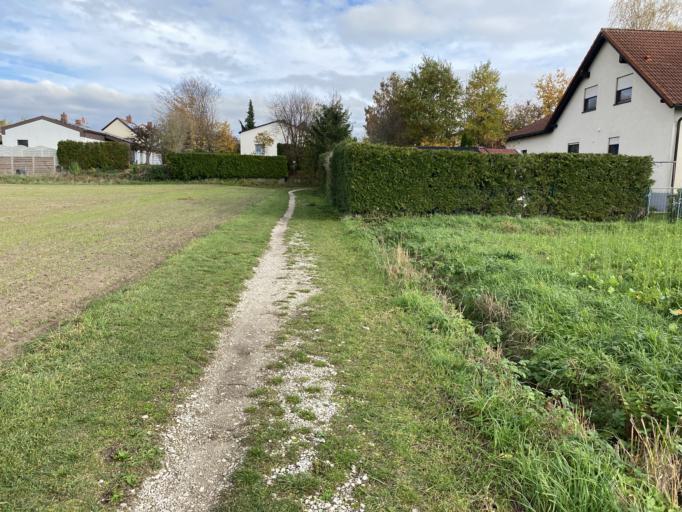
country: DE
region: Bavaria
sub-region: Upper Franconia
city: Poxdorf
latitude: 49.6556
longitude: 11.0566
